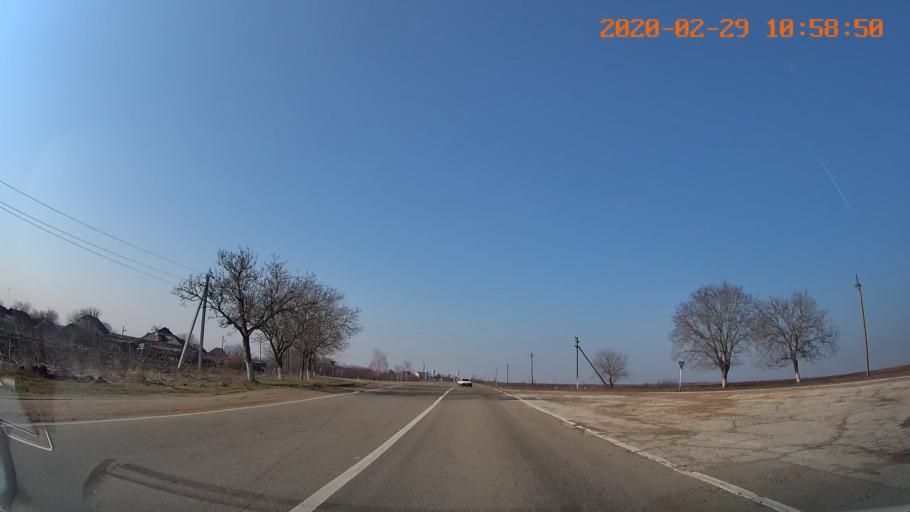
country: MD
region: Telenesti
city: Grigoriopol
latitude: 47.1654
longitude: 29.3030
